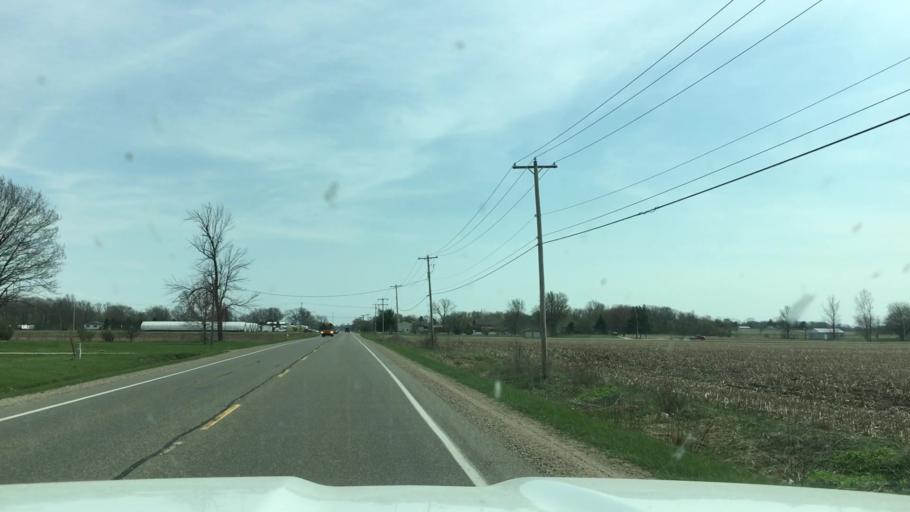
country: US
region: Michigan
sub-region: Ottawa County
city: Hudsonville
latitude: 42.8735
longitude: -85.9012
